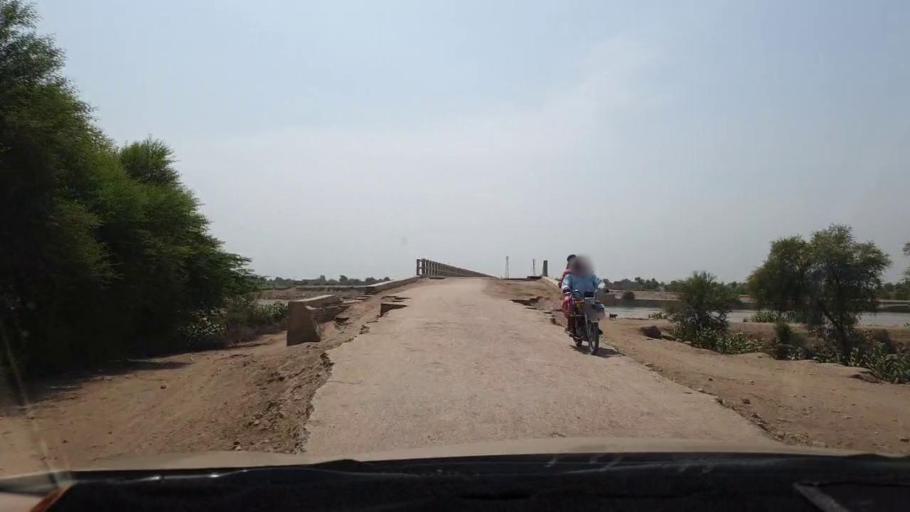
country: PK
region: Sindh
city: Larkana
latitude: 27.6248
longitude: 68.2744
